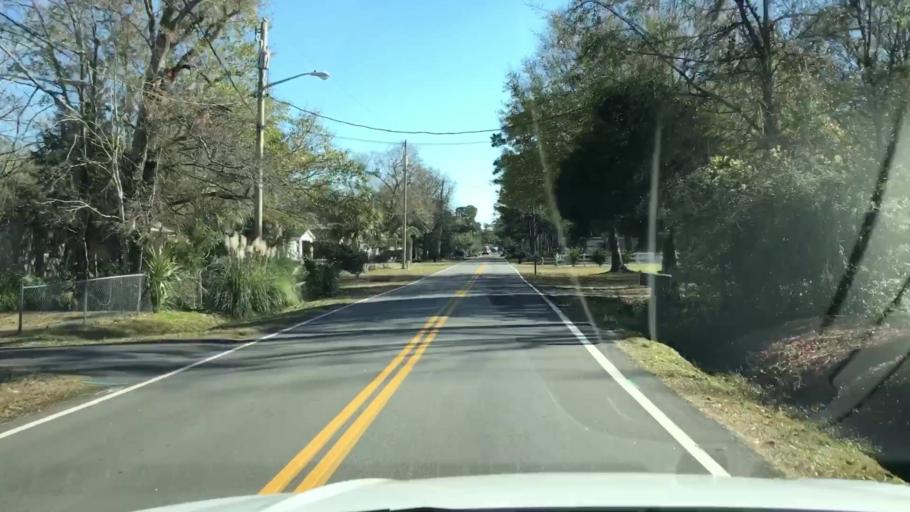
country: US
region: South Carolina
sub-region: Horry County
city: Garden City
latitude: 33.5935
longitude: -79.0004
